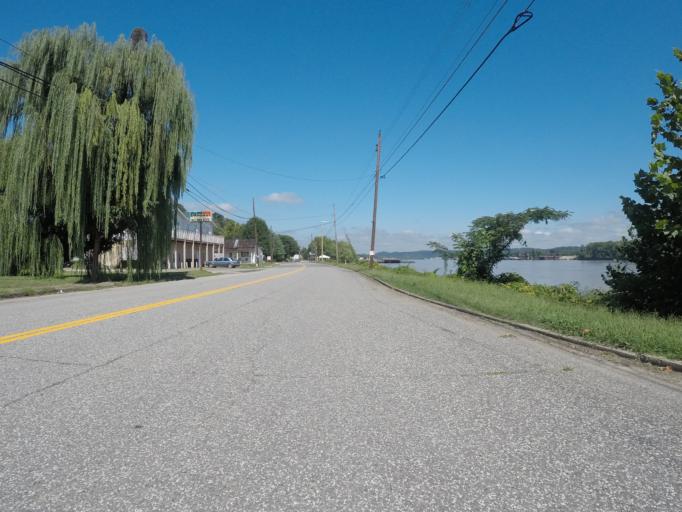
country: US
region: Ohio
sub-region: Lawrence County
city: South Point
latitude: 38.4246
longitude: -82.6004
